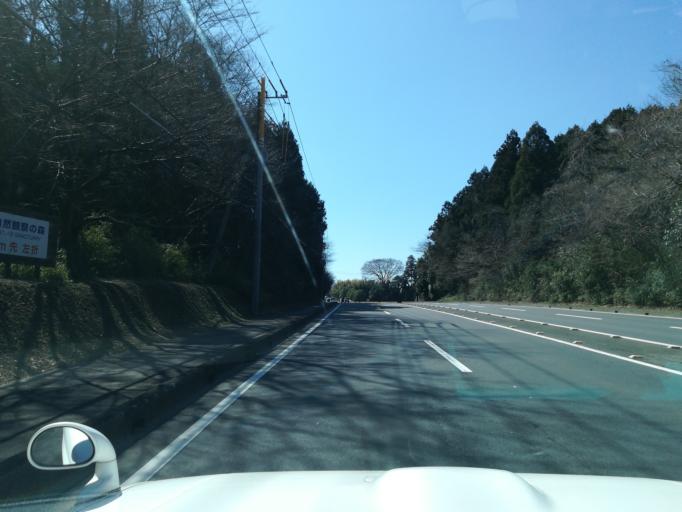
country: JP
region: Ibaraki
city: Ushiku
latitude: 35.9657
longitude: 140.1711
